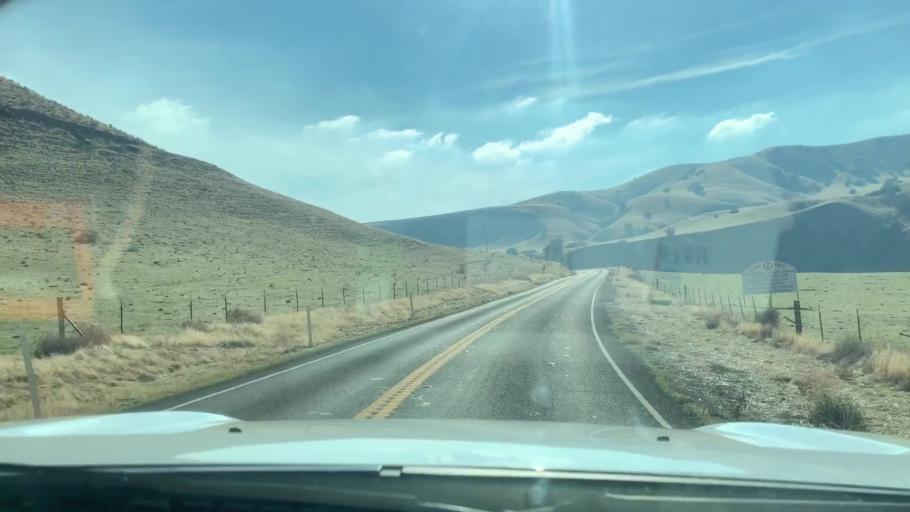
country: US
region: California
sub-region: Fresno County
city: Coalinga
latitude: 36.0960
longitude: -120.4359
